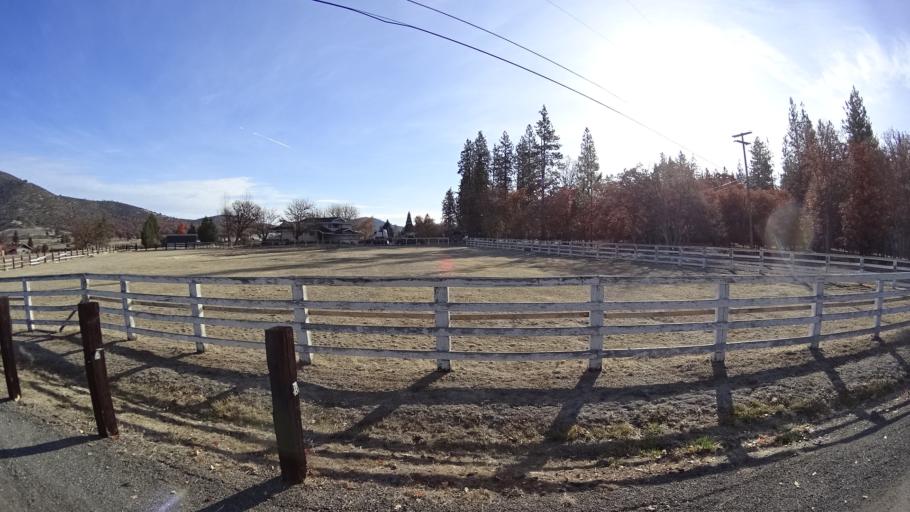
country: US
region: California
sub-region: Siskiyou County
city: Yreka
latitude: 41.6745
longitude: -122.6354
